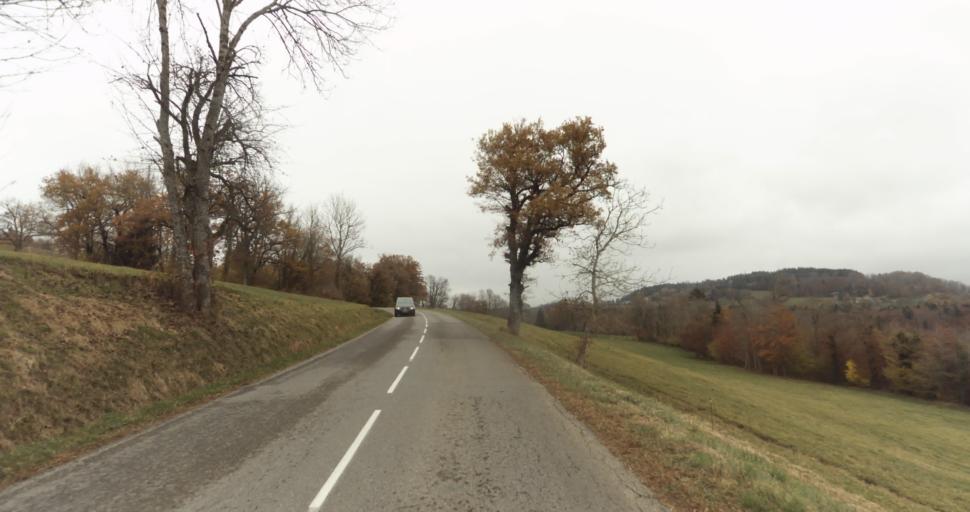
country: FR
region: Rhone-Alpes
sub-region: Departement de la Haute-Savoie
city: Evires
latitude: 46.0287
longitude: 6.2064
